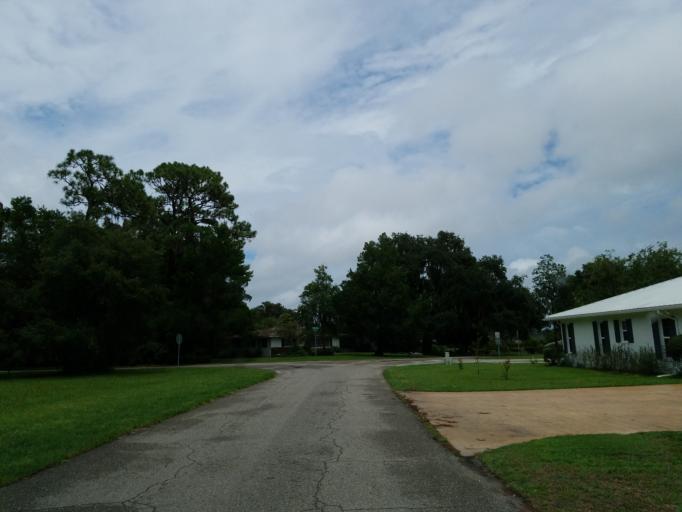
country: US
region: Florida
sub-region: Citrus County
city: Inverness
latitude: 28.8170
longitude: -82.2893
